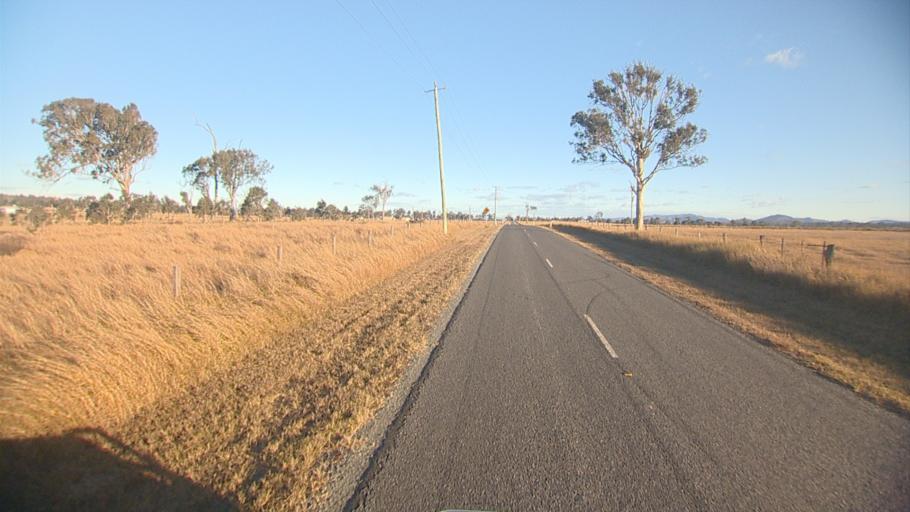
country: AU
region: Queensland
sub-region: Logan
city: Cedar Vale
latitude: -27.8690
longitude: 152.9574
